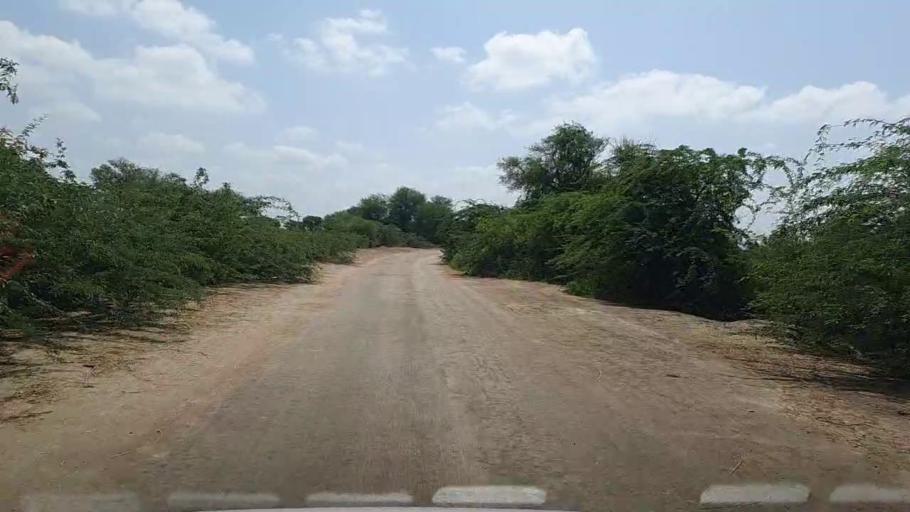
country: PK
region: Sindh
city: Talhar
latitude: 24.8905
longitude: 68.7017
